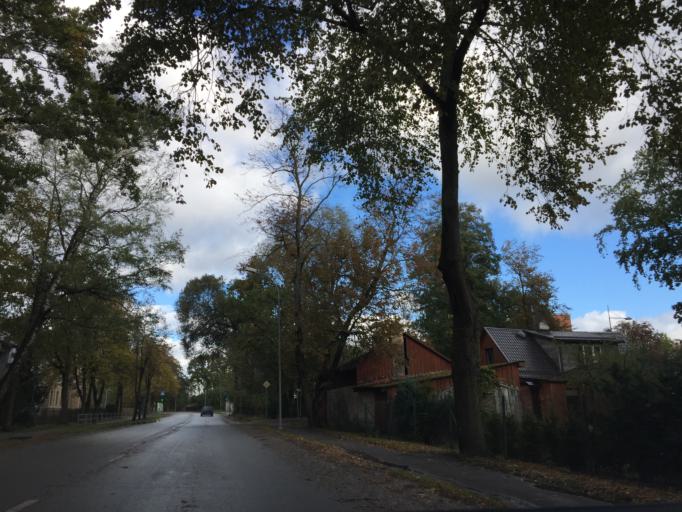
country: LV
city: Tireli
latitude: 56.9480
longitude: 23.6134
